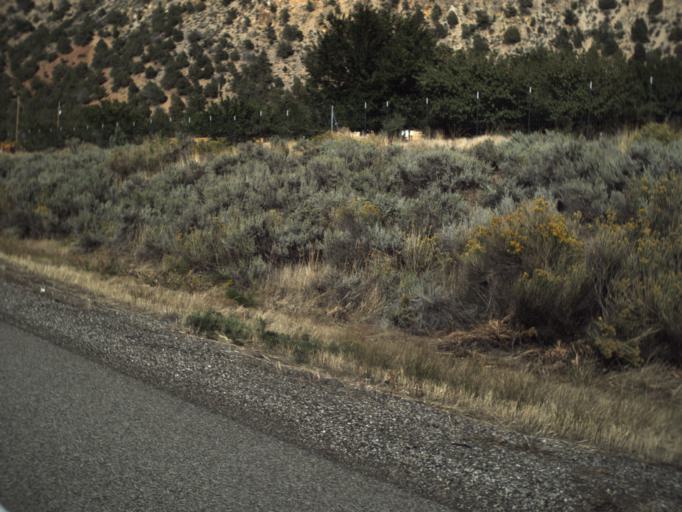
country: US
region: Utah
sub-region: Washington County
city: Toquerville
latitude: 37.4794
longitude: -113.2209
